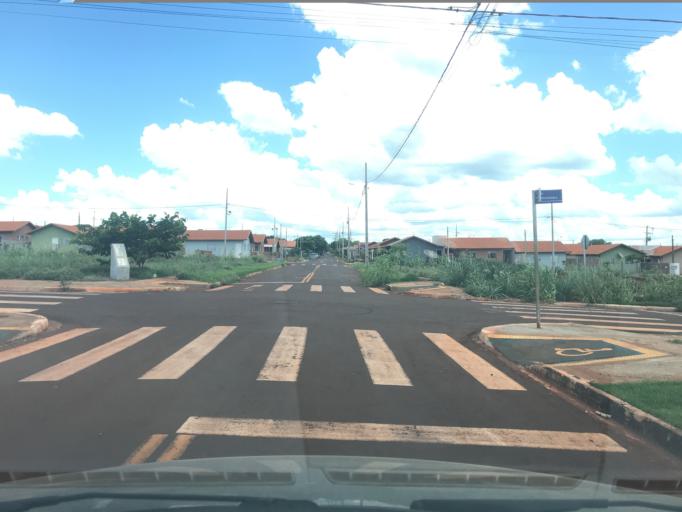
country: BR
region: Parana
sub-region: Palotina
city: Palotina
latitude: -24.2655
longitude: -53.8463
